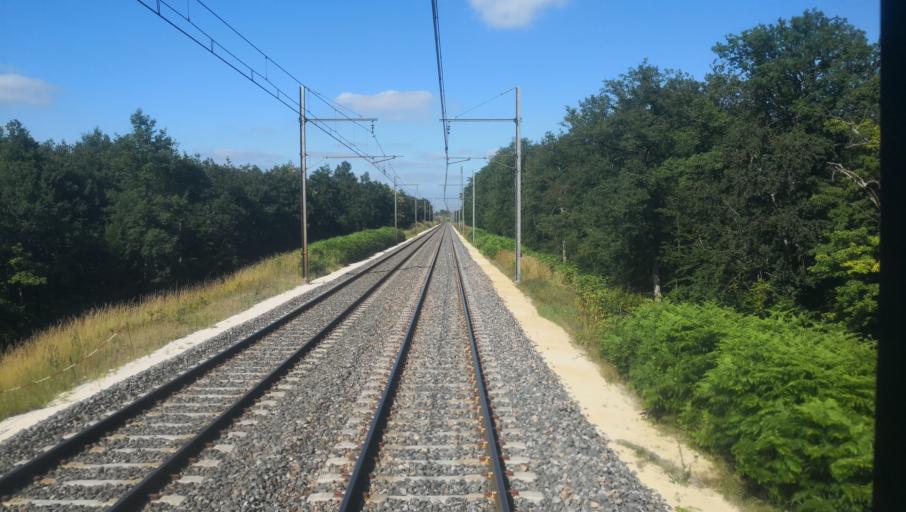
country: FR
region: Ile-de-France
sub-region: Departement de Seine-et-Marne
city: Veneux-les-Sablons
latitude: 48.3579
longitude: 2.7964
